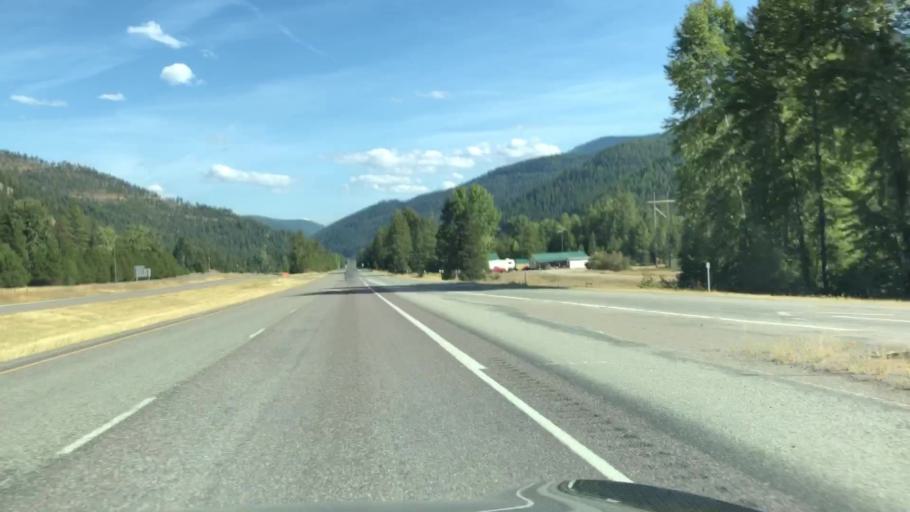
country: US
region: Montana
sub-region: Sanders County
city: Thompson Falls
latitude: 47.3744
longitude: -115.3472
